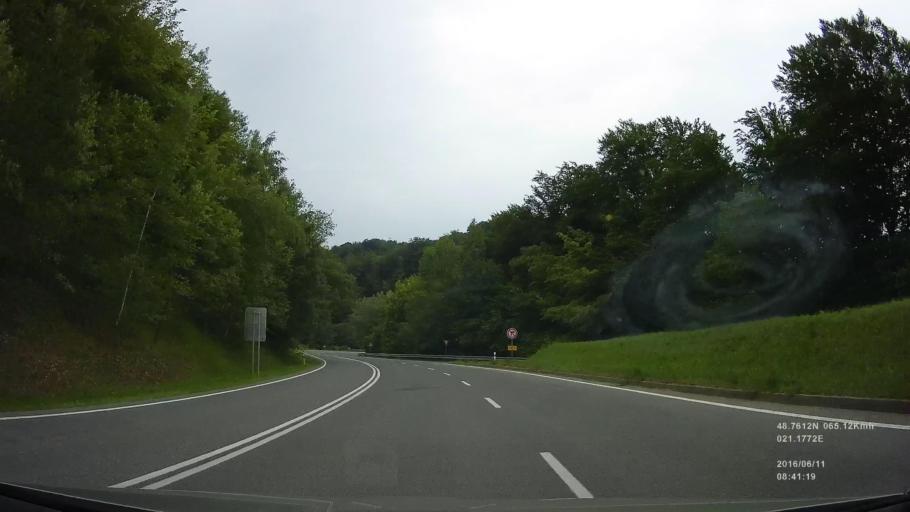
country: SK
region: Kosicky
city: Kosice
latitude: 48.7511
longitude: 21.2248
